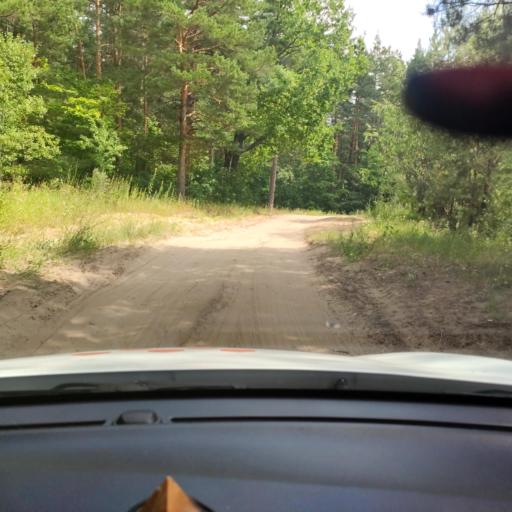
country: RU
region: Tatarstan
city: Osinovo
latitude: 55.9114
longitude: 48.9621
